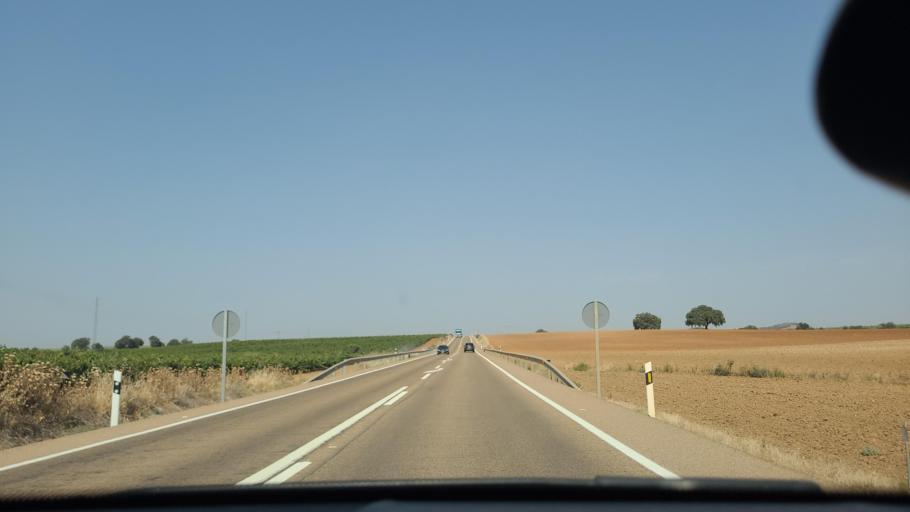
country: ES
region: Extremadura
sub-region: Provincia de Badajoz
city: Bienvenida
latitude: 38.3744
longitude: -6.2579
